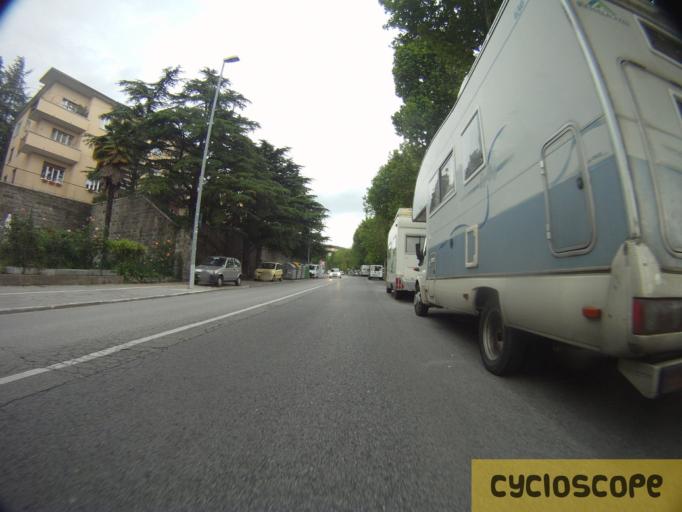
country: IT
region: Friuli Venezia Giulia
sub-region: Provincia di Trieste
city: Trieste
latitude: 45.6418
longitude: 13.8043
